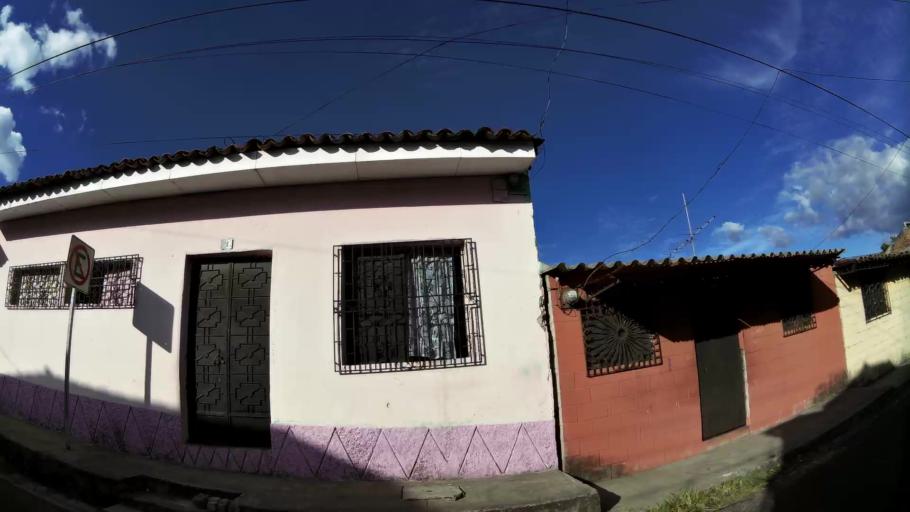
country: SV
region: Cuscatlan
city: Cojutepeque
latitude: 13.7208
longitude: -88.9370
